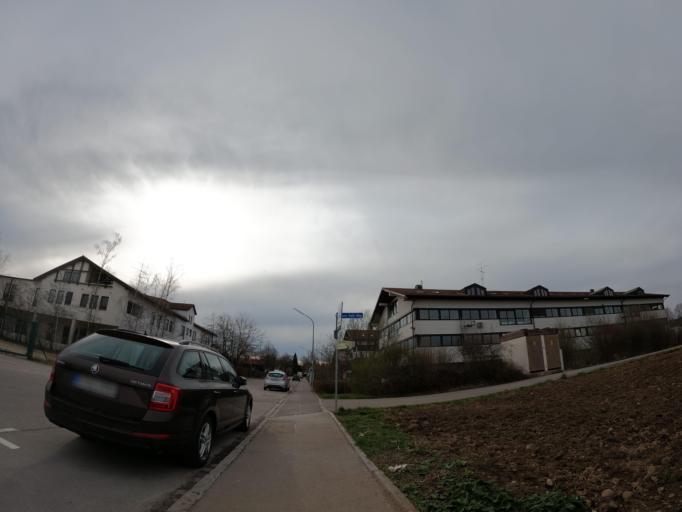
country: DE
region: Bavaria
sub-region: Upper Bavaria
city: Taufkirchen
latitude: 48.0331
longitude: 11.6179
